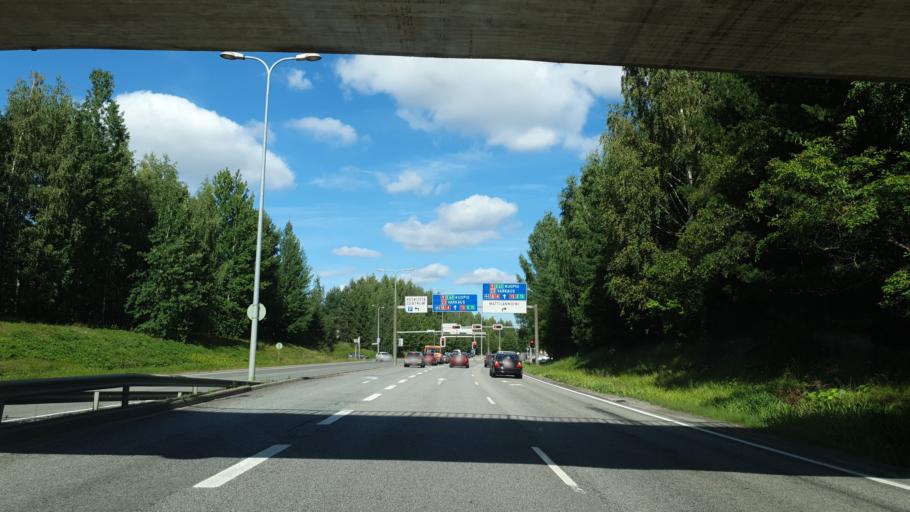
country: FI
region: Central Finland
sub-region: Jyvaeskylae
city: Jyvaeskylae
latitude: 62.2315
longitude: 25.7329
